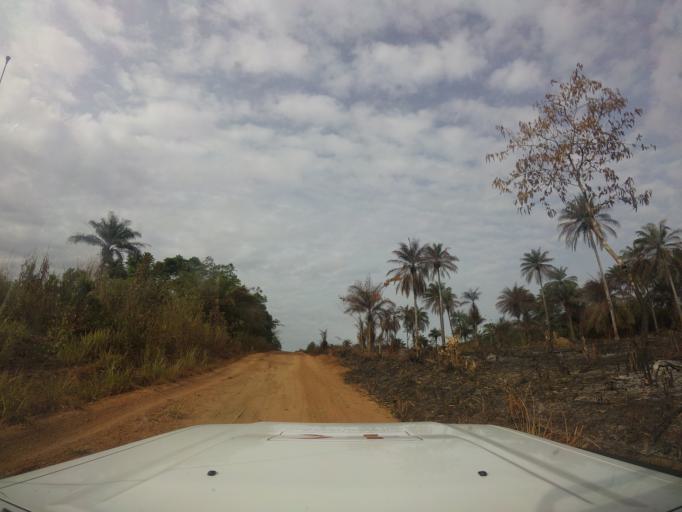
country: LR
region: Grand Cape Mount
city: Robertsport
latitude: 6.9609
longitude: -11.3175
